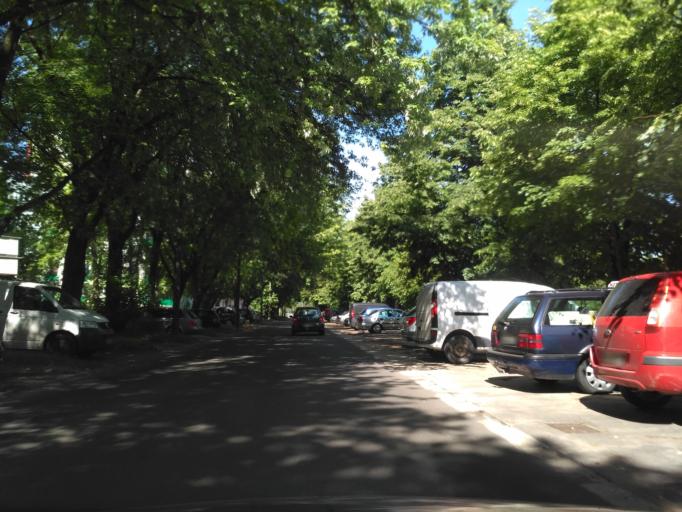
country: PL
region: Lublin Voivodeship
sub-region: Powiat lubelski
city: Lublin
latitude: 51.2630
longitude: 22.5477
